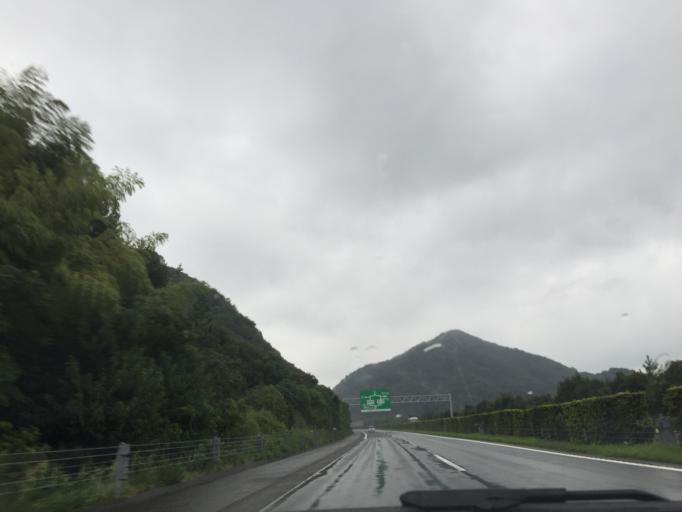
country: JP
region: Tokushima
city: Narutocho-mitsuishi
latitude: 34.2159
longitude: 134.6242
